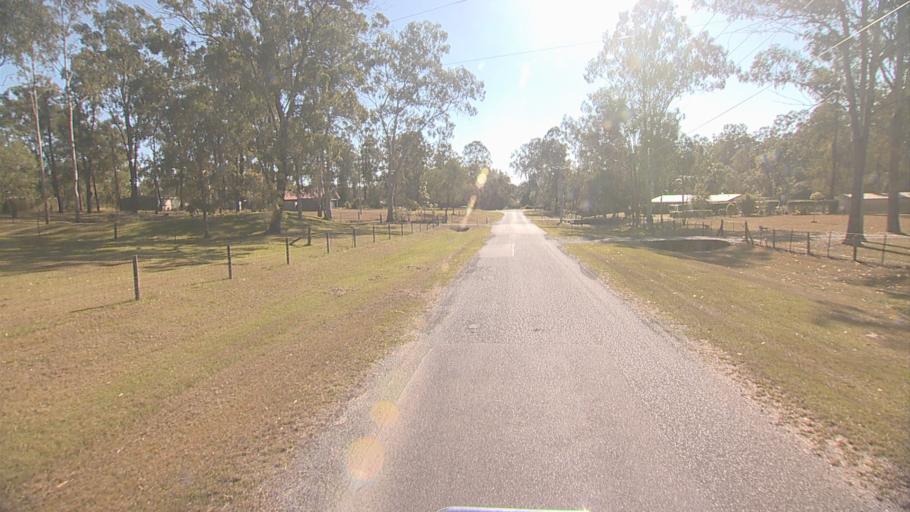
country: AU
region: Queensland
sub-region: Logan
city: Cedar Vale
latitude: -27.8259
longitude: 153.0481
